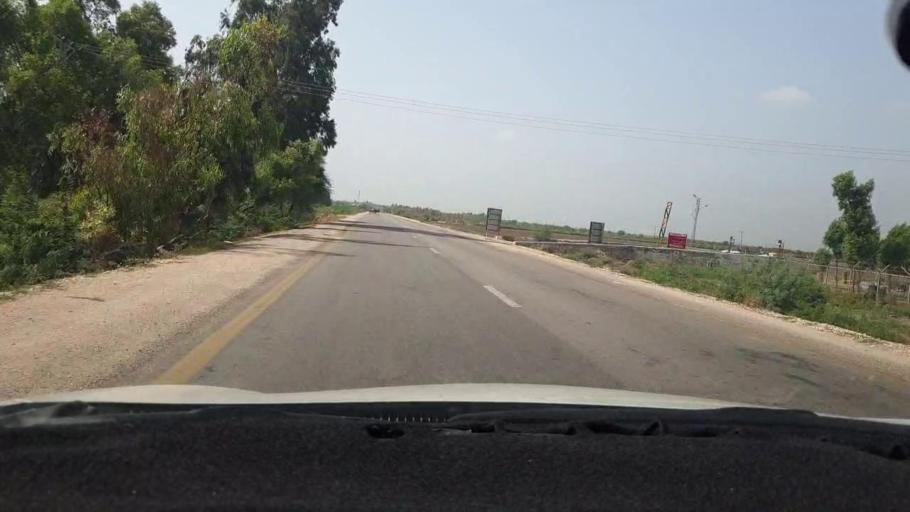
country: PK
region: Sindh
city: Mirpur Khas
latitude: 25.6777
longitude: 69.1090
